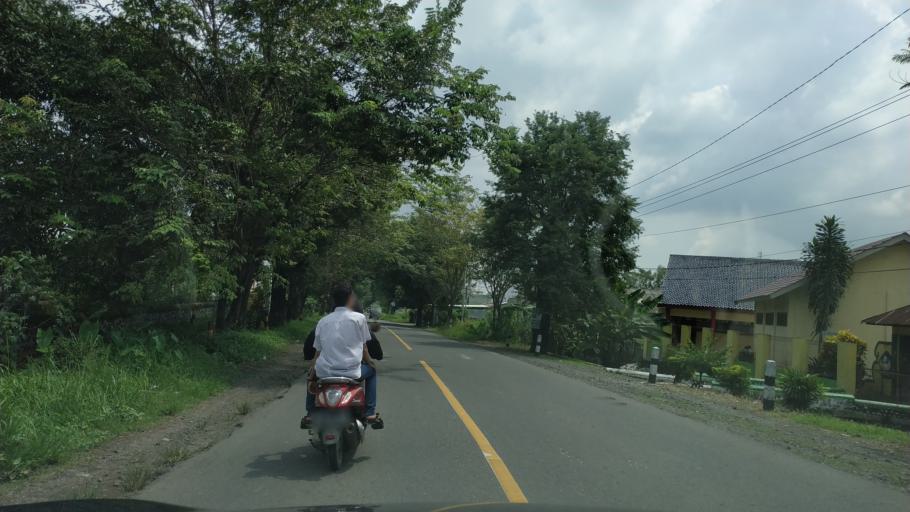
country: ID
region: Central Java
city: Lebaksiu
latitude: -7.0337
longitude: 109.1454
